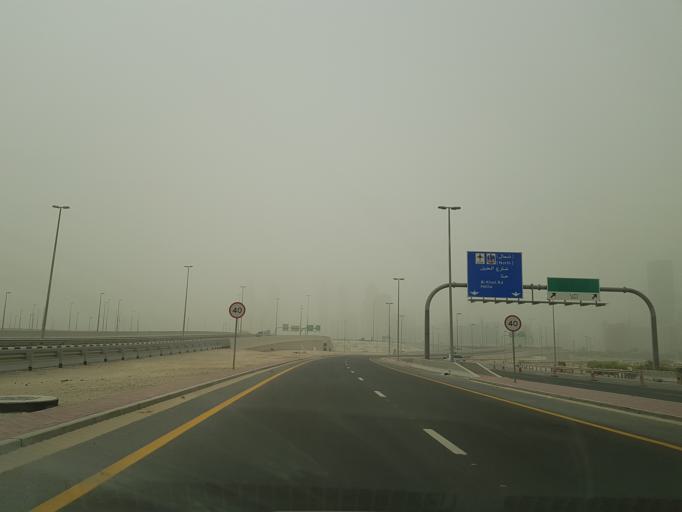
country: AE
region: Dubai
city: Dubai
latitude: 25.1667
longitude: 55.2710
